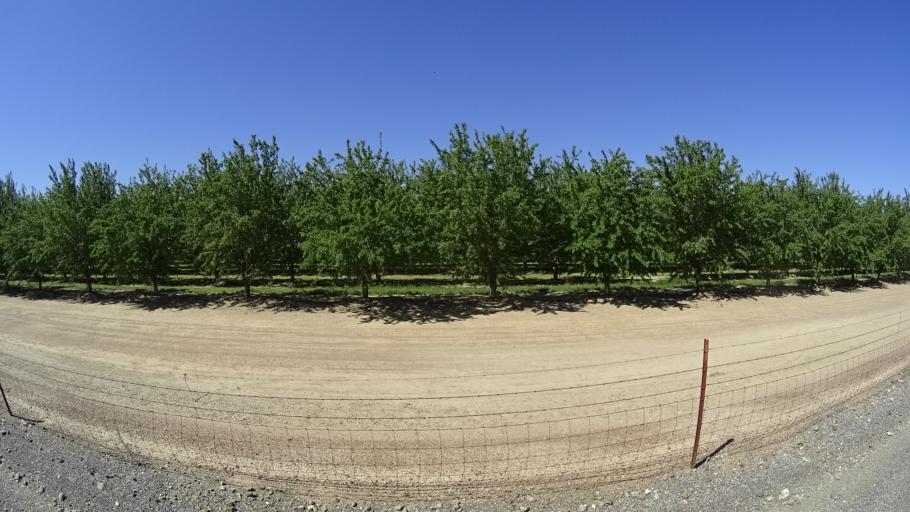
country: US
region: California
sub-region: Glenn County
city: Orland
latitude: 39.6669
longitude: -122.2344
